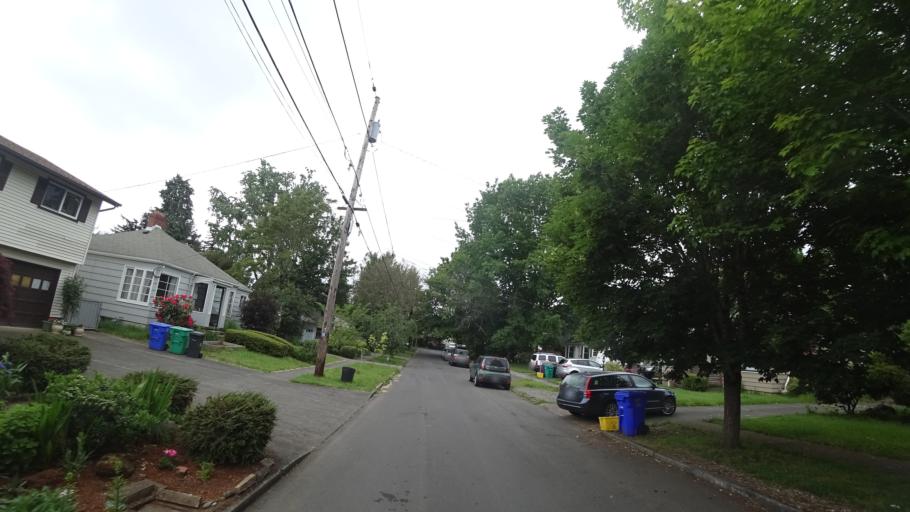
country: US
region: Oregon
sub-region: Multnomah County
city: Lents
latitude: 45.4910
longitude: -122.6140
